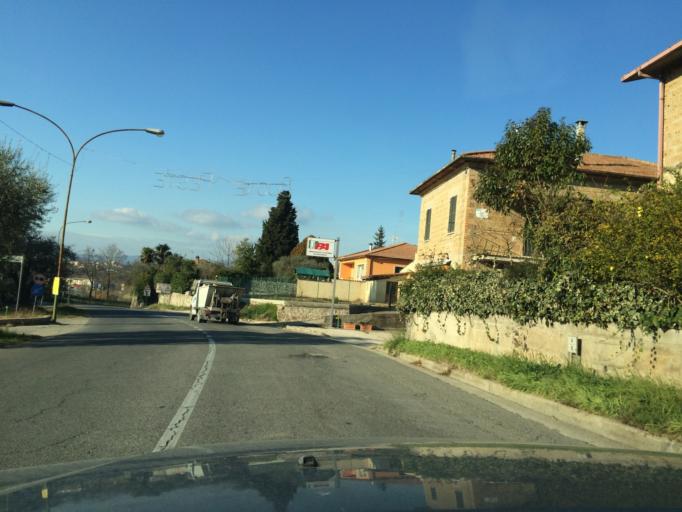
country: IT
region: Umbria
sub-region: Provincia di Terni
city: Fornole
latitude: 42.5432
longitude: 12.4547
